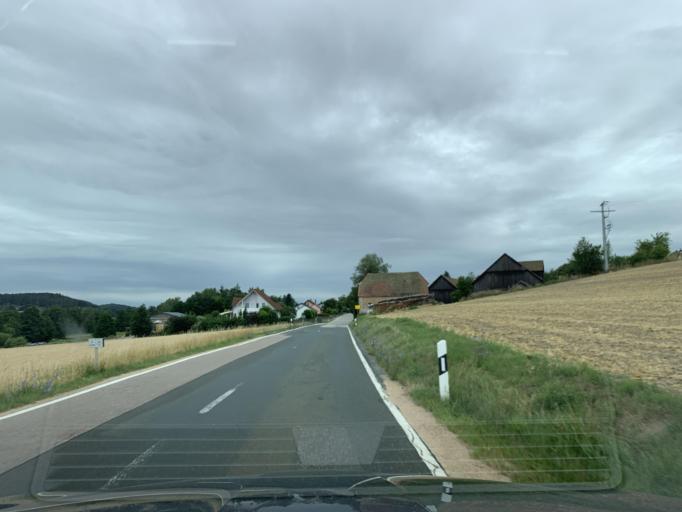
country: DE
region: Bavaria
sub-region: Upper Palatinate
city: Schwarzhofen
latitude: 49.3719
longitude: 12.3484
